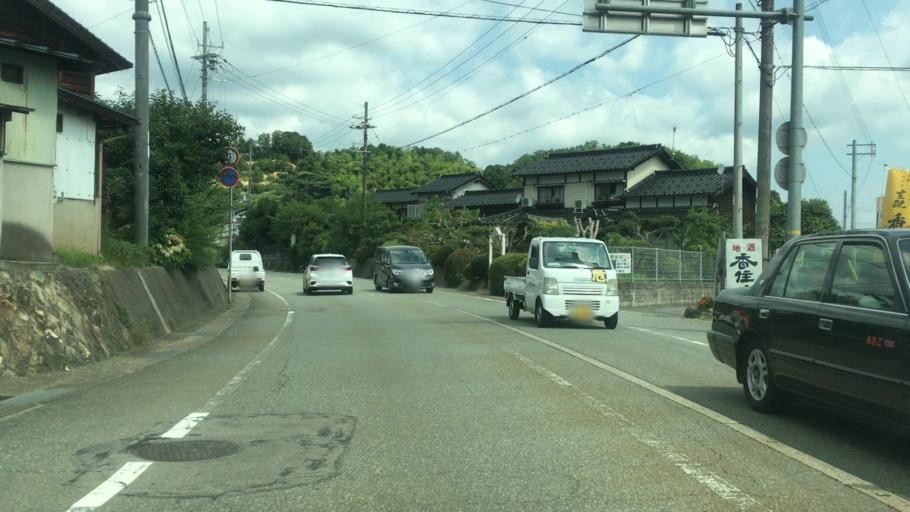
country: JP
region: Hyogo
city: Toyooka
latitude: 35.5531
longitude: 134.8059
